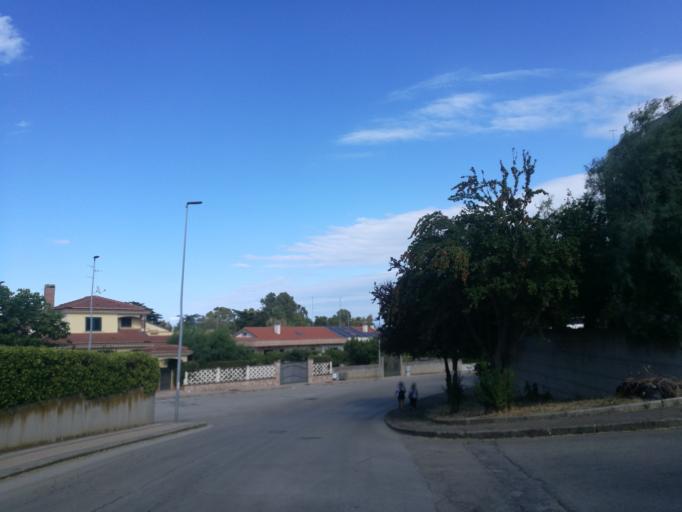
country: IT
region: Molise
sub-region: Provincia di Campobasso
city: Termoli
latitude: 41.9824
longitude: 14.9821
